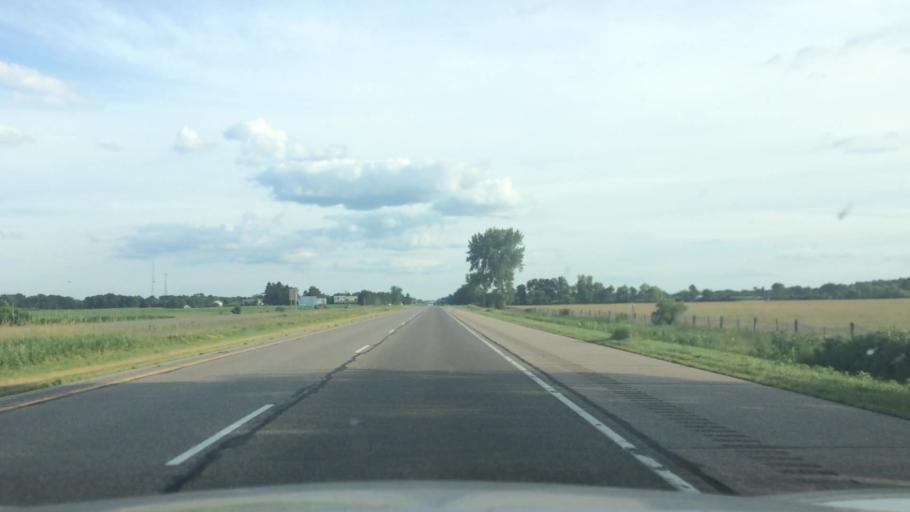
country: US
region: Wisconsin
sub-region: Portage County
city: Plover
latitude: 44.3250
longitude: -89.5235
